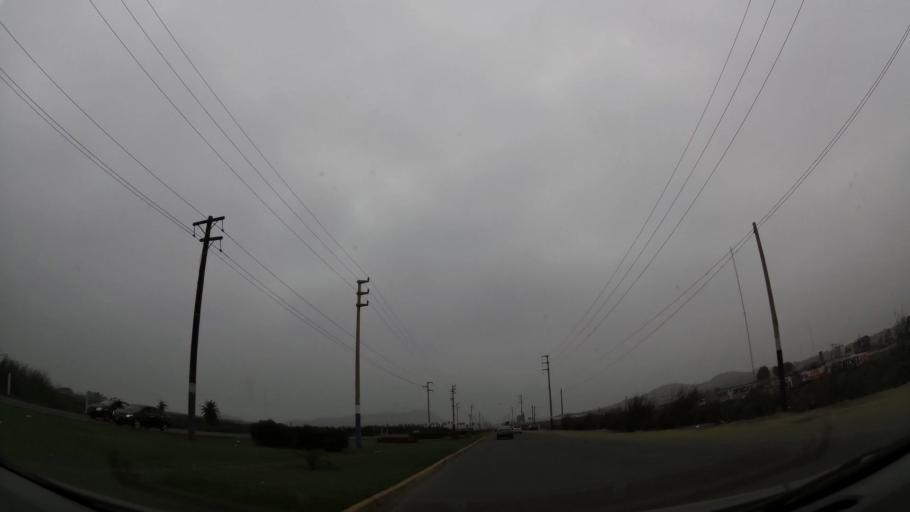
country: PE
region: Lima
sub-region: Lima
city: Surco
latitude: -12.2140
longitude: -76.9828
